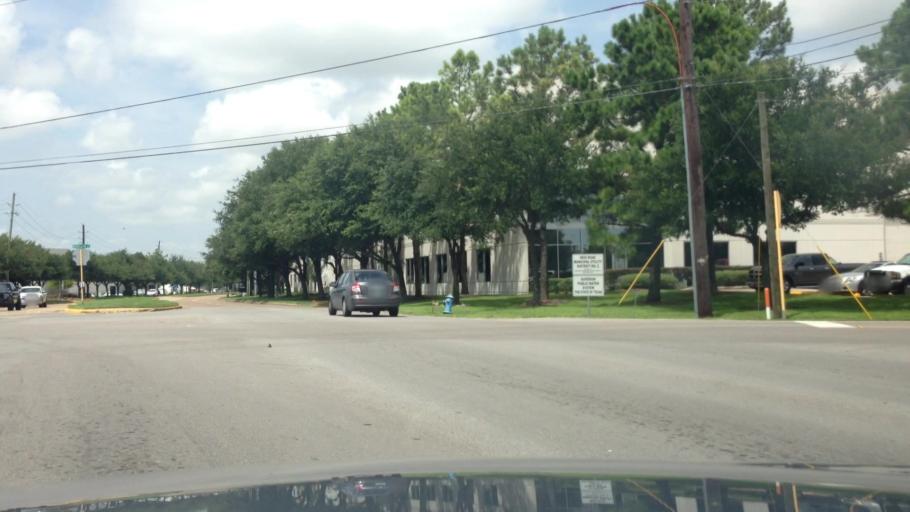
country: US
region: Texas
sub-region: Harris County
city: Jersey Village
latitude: 29.9258
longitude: -95.5478
